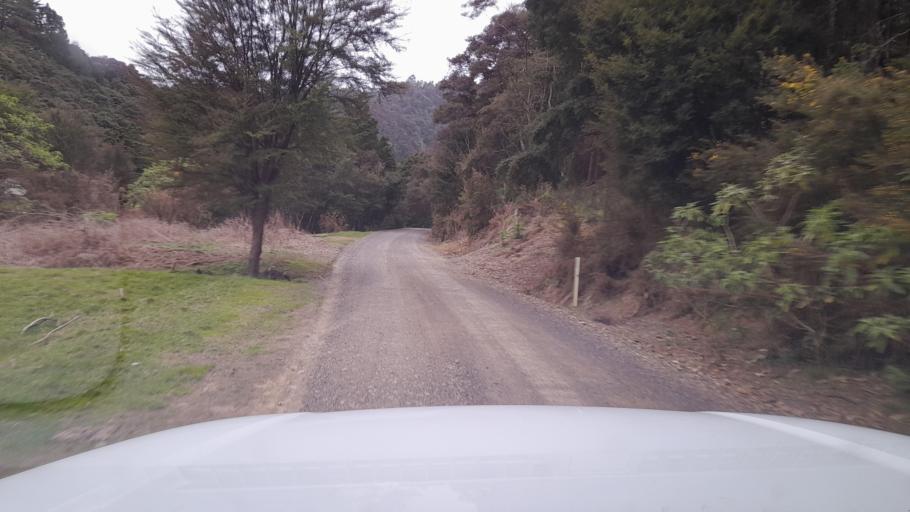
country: NZ
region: Northland
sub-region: Far North District
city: Paihia
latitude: -35.3544
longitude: 174.2328
